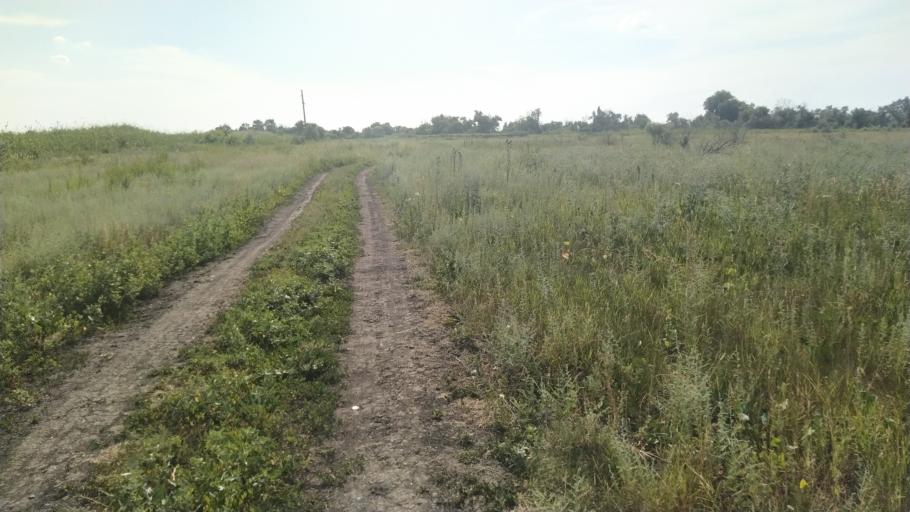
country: RU
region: Rostov
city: Kuleshovka
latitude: 47.1277
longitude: 39.6134
